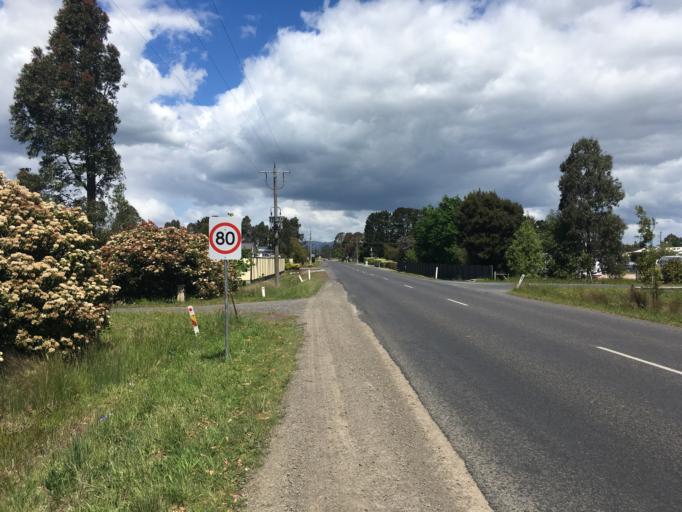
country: AU
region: Victoria
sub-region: Latrobe
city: Traralgon
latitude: -38.2138
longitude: 146.4764
